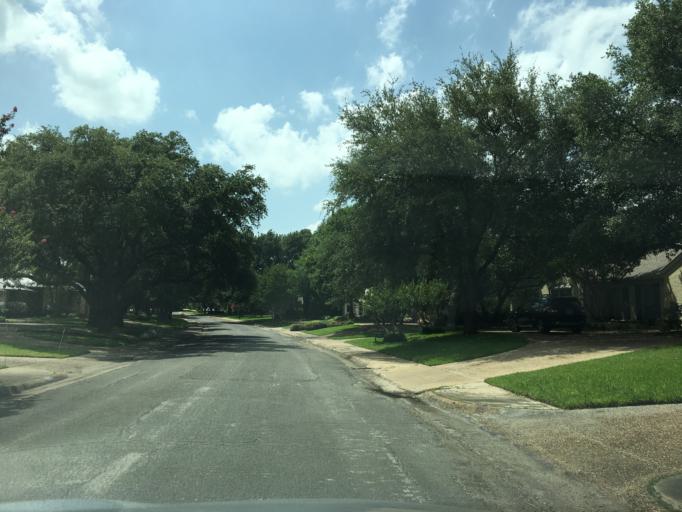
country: US
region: Texas
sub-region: Dallas County
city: University Park
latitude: 32.8762
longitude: -96.7834
